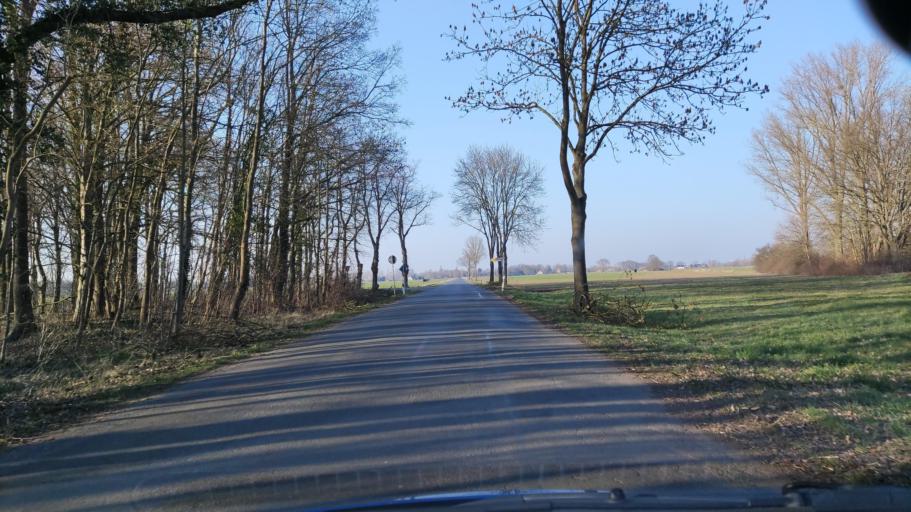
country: DE
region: Brandenburg
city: Wittenberge
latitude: 52.9550
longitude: 11.7482
